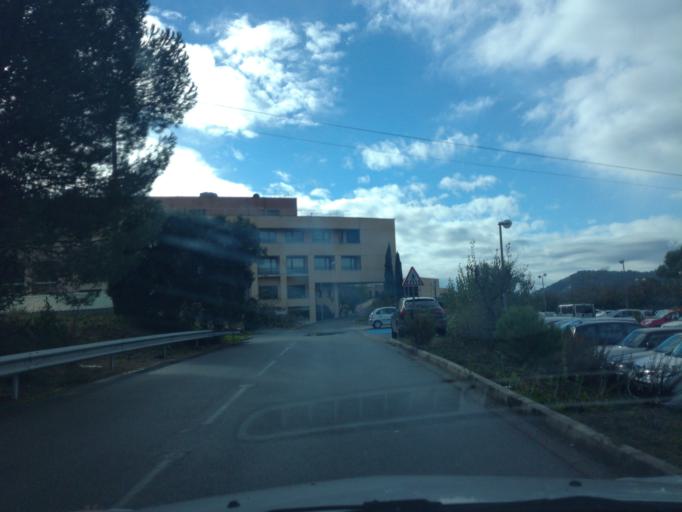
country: FR
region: Provence-Alpes-Cote d'Azur
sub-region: Departement des Alpes-Maritimes
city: Pegomas
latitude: 43.6214
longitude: 6.9314
